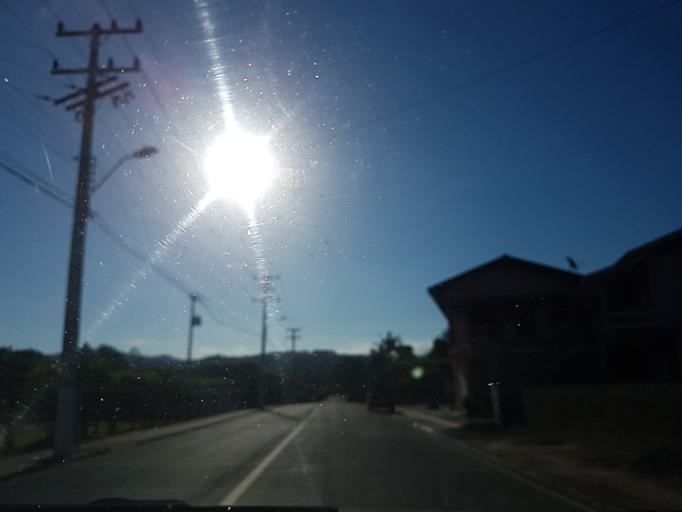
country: BR
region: Santa Catarina
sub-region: Braco Do Norte
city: Braco do Norte
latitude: -28.3301
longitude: -49.1675
